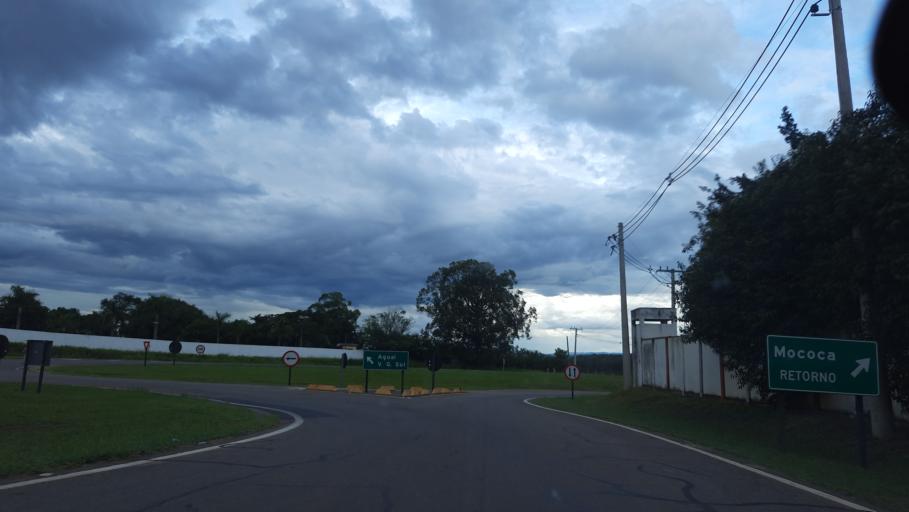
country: BR
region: Sao Paulo
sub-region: Casa Branca
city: Casa Branca
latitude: -21.7700
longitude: -47.0675
